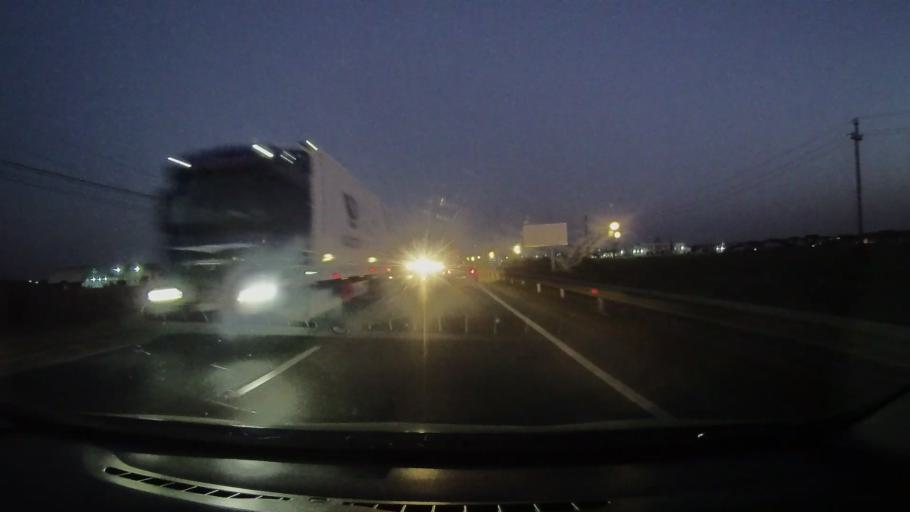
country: RO
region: Arad
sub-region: Comuna Vladimirescu
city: Vladimirescu
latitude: 46.1695
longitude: 21.3858
